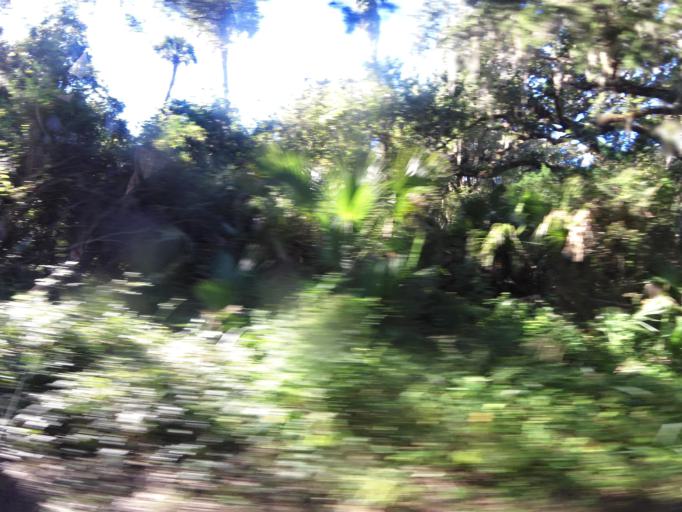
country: US
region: Florida
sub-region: Duval County
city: Atlantic Beach
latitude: 30.4174
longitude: -81.4275
